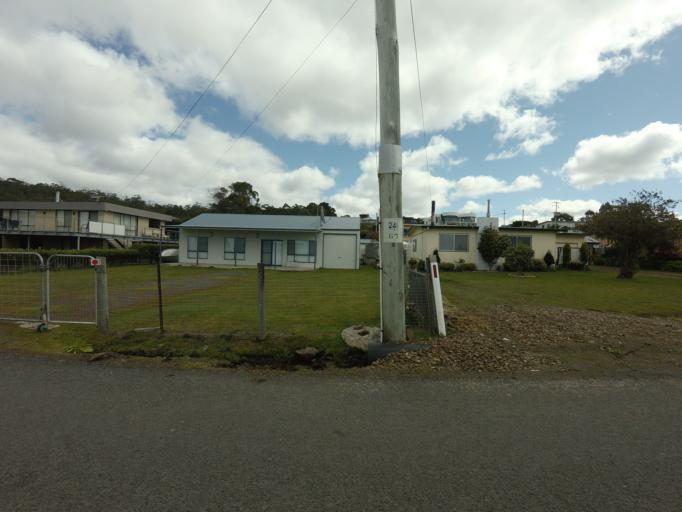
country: AU
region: Tasmania
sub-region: Huon Valley
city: Geeveston
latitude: -43.4398
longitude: 146.9613
